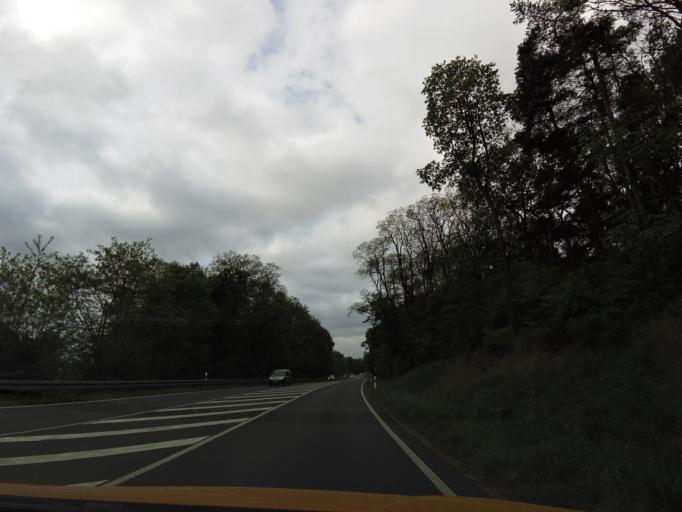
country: DE
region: Brandenburg
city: Michendorf
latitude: 52.2955
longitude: 13.0242
